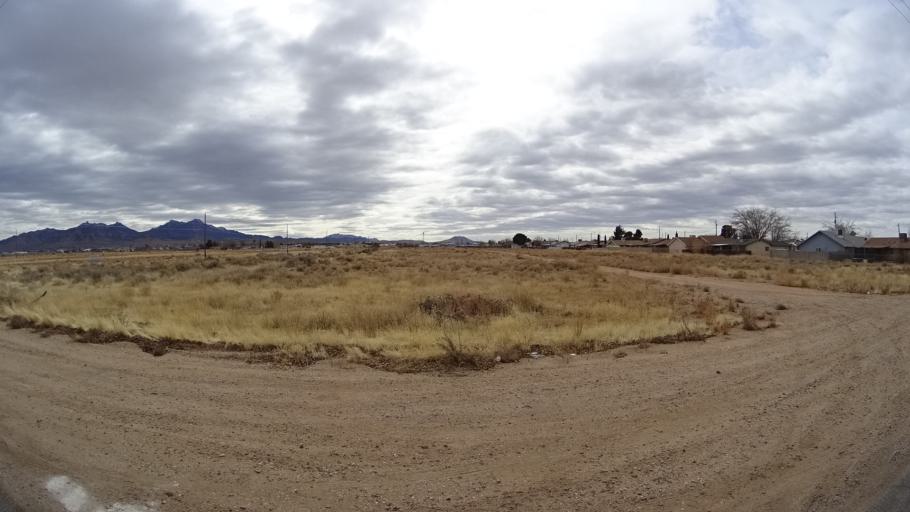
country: US
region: Arizona
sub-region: Mohave County
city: New Kingman-Butler
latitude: 35.2322
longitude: -114.0173
